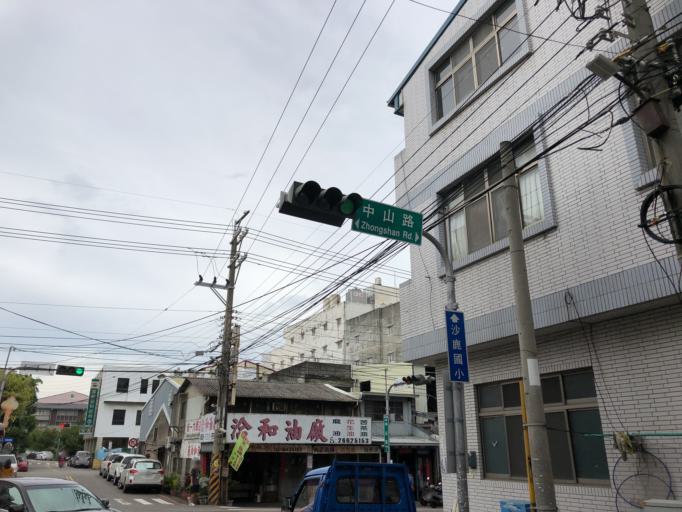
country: TW
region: Taiwan
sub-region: Taichung City
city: Taichung
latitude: 24.2379
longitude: 120.5622
